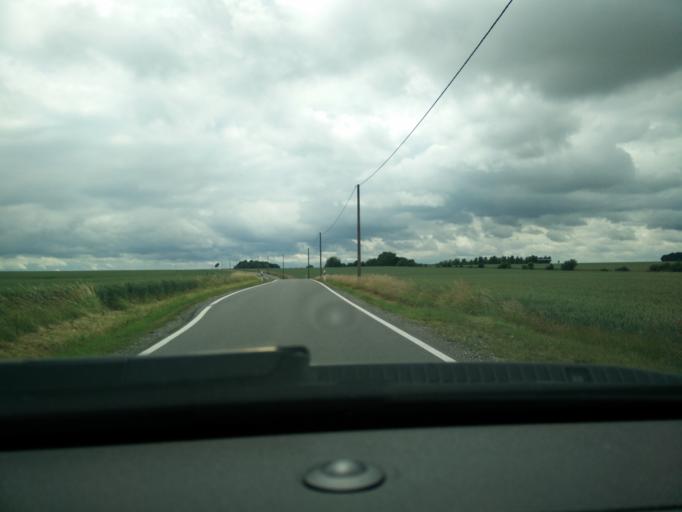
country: DE
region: Saxony
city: Bad Lausick
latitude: 51.1232
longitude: 12.6606
